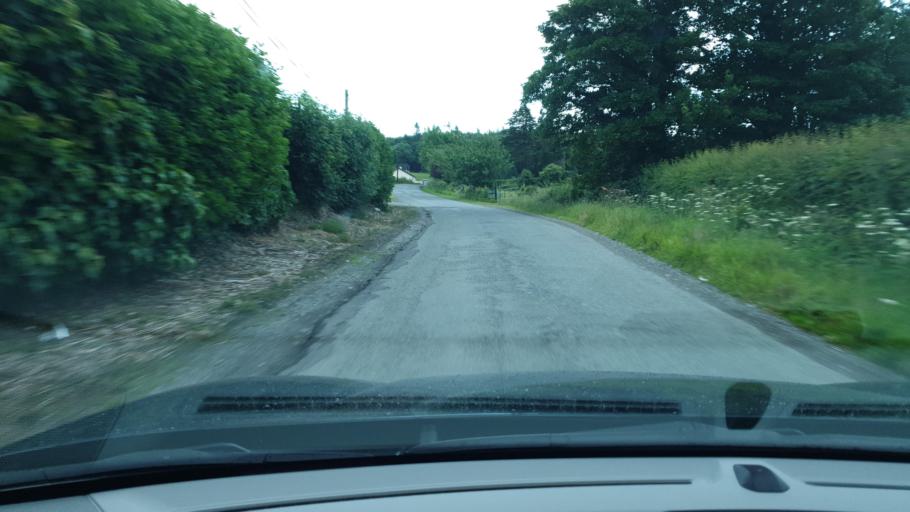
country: IE
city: Kentstown
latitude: 53.5978
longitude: -6.5848
